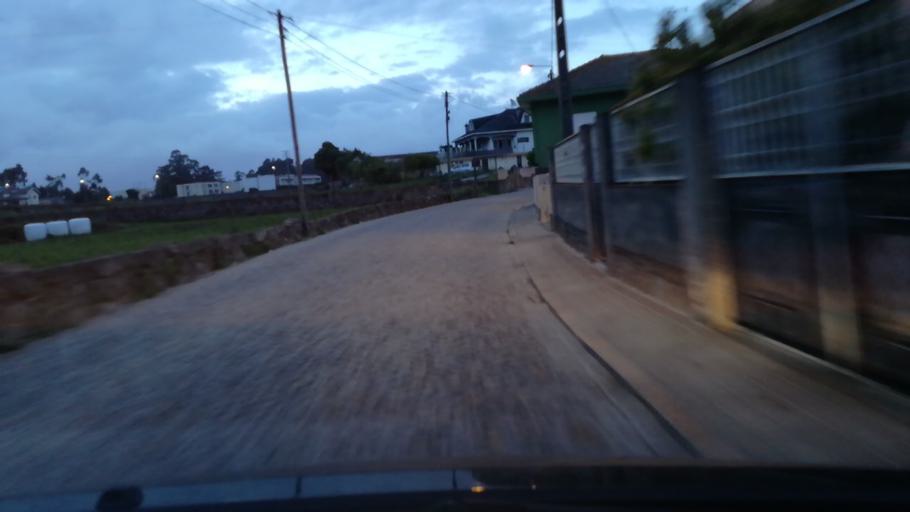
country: PT
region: Porto
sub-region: Maia
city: Maia
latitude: 41.2527
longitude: -8.6091
